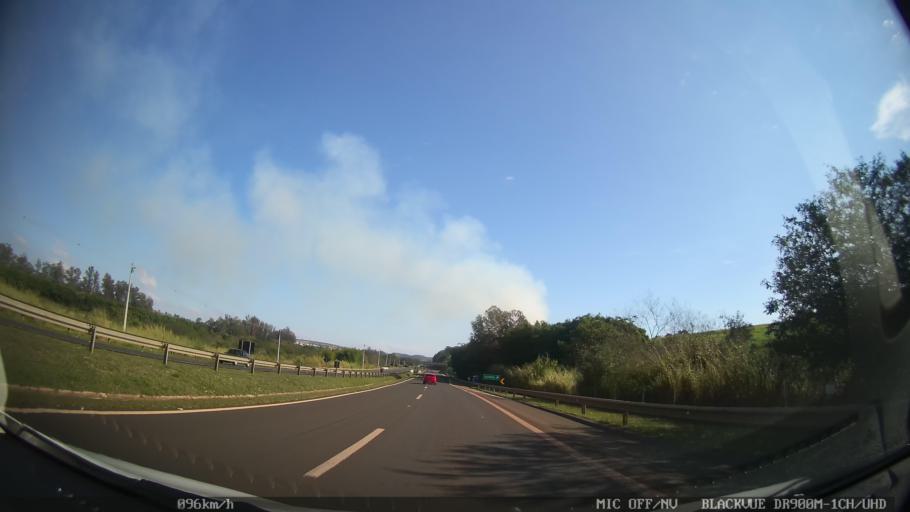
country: BR
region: Sao Paulo
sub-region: Piracicaba
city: Piracicaba
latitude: -22.6843
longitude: -47.5801
